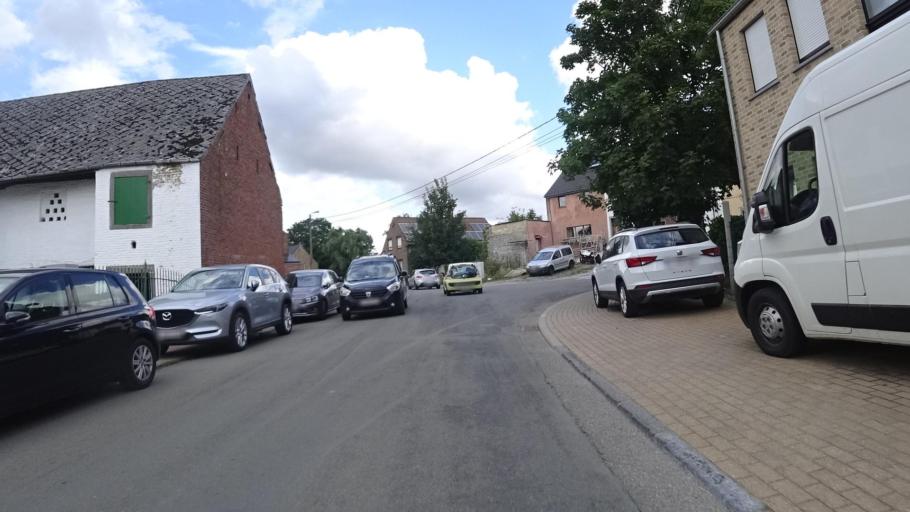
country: BE
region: Wallonia
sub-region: Province du Brabant Wallon
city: Villers-la-Ville
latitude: 50.5498
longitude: 4.5542
